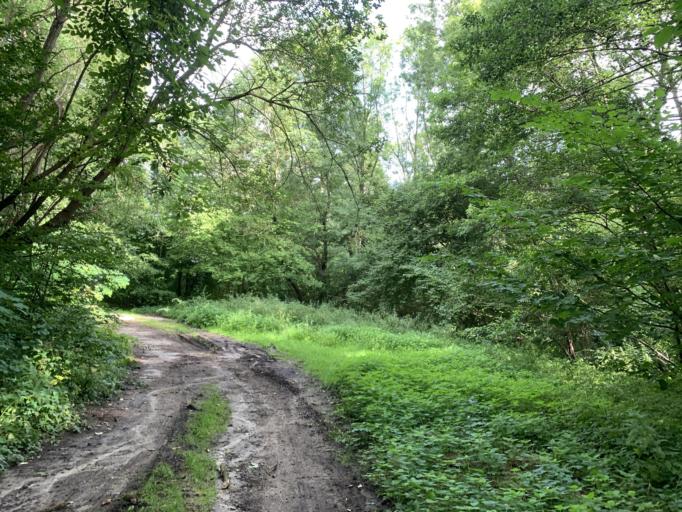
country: DE
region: Mecklenburg-Vorpommern
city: Gross Nemerow
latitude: 53.4250
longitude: 13.1887
